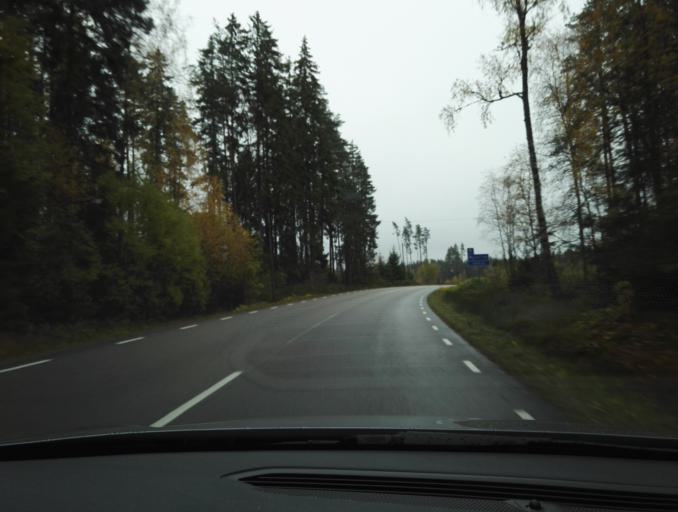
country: SE
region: Kronoberg
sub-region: Vaxjo Kommun
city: Rottne
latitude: 57.0270
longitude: 14.8276
